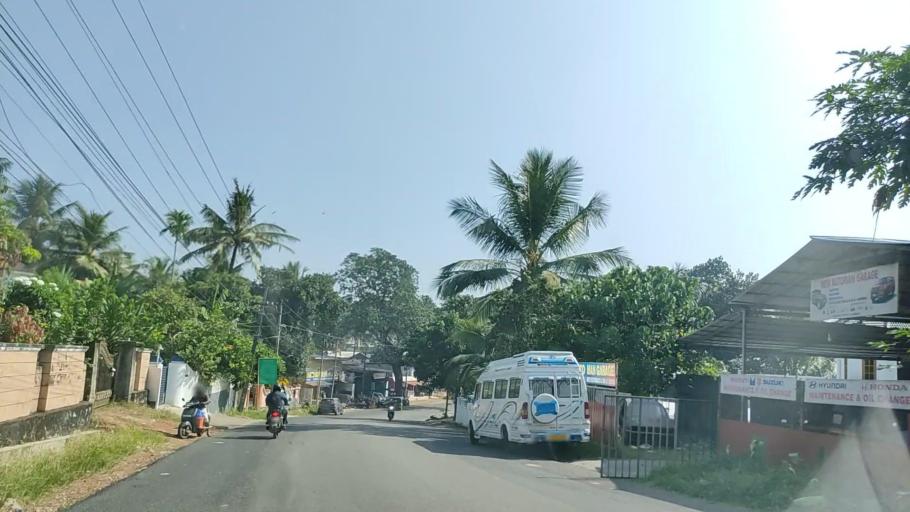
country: IN
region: Kerala
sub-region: Kollam
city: Punalur
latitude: 8.9292
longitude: 76.9279
